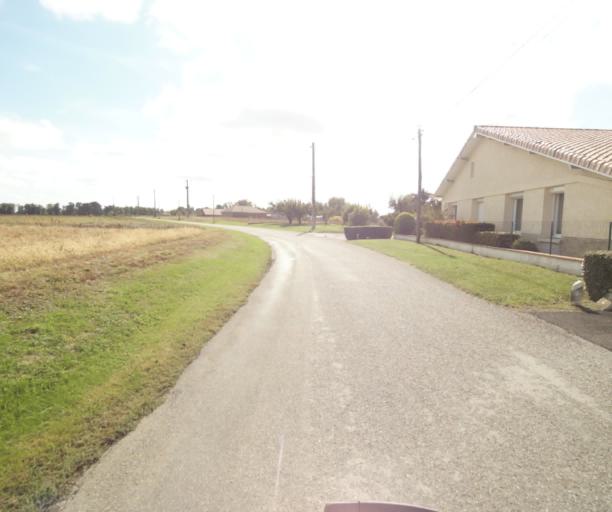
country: FR
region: Midi-Pyrenees
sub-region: Departement du Tarn-et-Garonne
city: Finhan
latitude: 43.9335
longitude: 1.2151
